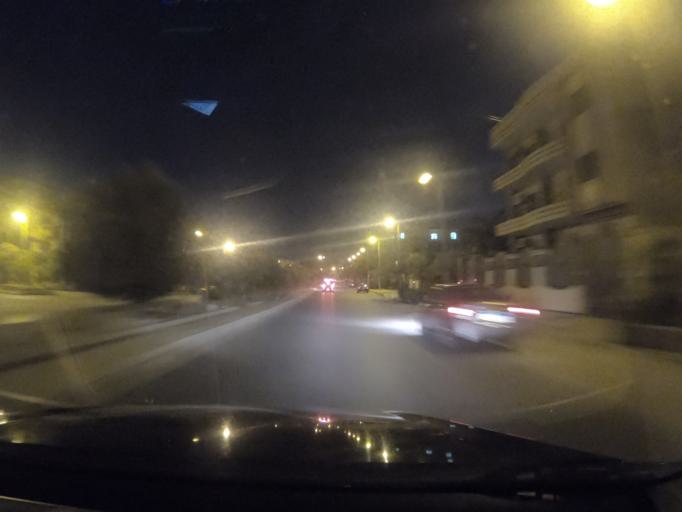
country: EG
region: Muhafazat al Qahirah
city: Cairo
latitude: 30.0120
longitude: 31.4184
